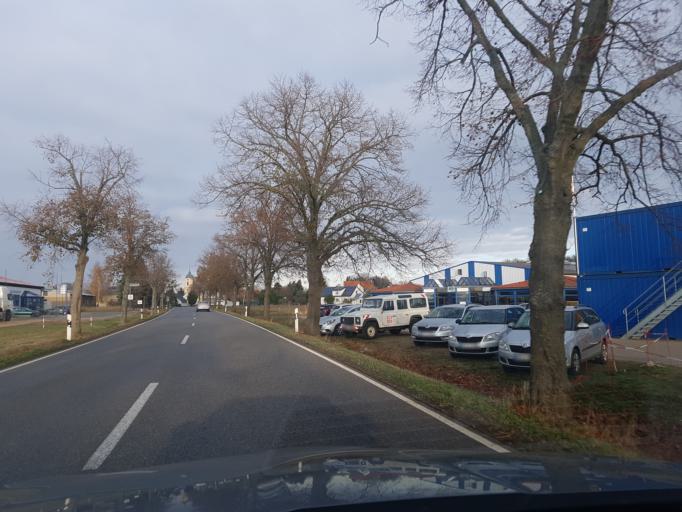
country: DE
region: Brandenburg
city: Golssen
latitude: 51.9466
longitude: 13.6477
